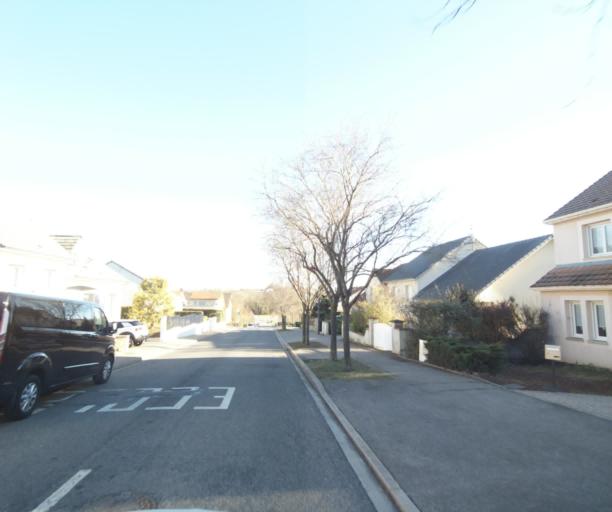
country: FR
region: Lorraine
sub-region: Departement de Meurthe-et-Moselle
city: Heillecourt
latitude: 48.6568
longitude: 6.2185
